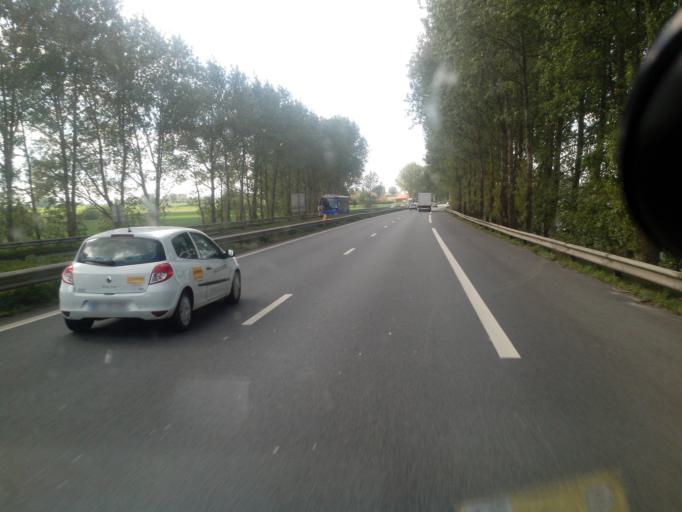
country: FR
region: Nord-Pas-de-Calais
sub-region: Departement du Nord
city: Bierne
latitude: 50.9518
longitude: 2.4204
